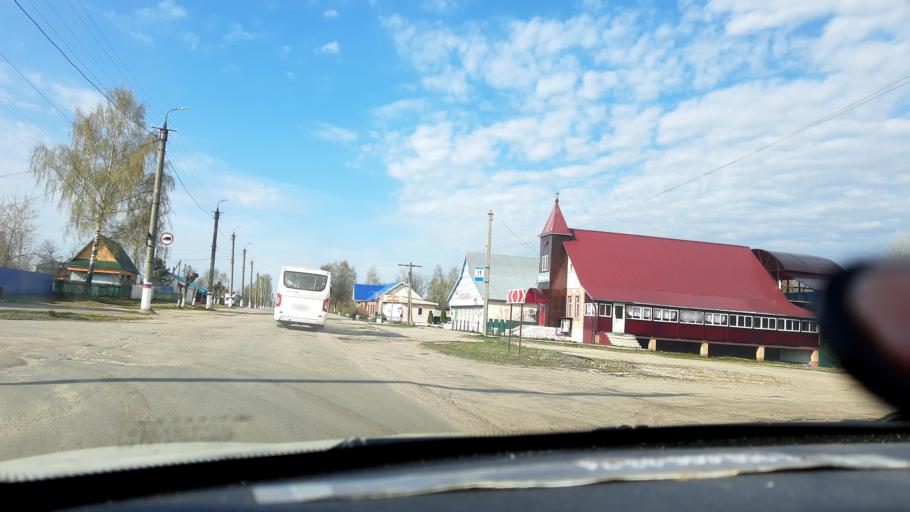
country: RU
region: Mariy-El
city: Kilemary
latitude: 56.7830
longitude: 46.8643
